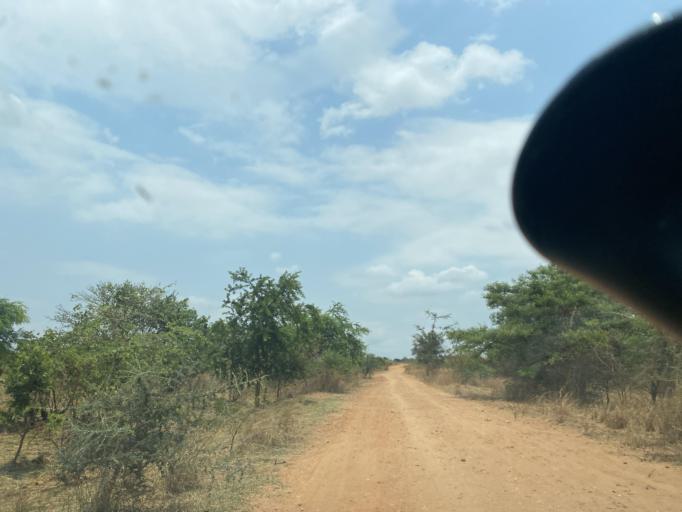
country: ZM
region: Lusaka
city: Chongwe
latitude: -15.5335
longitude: 28.8262
